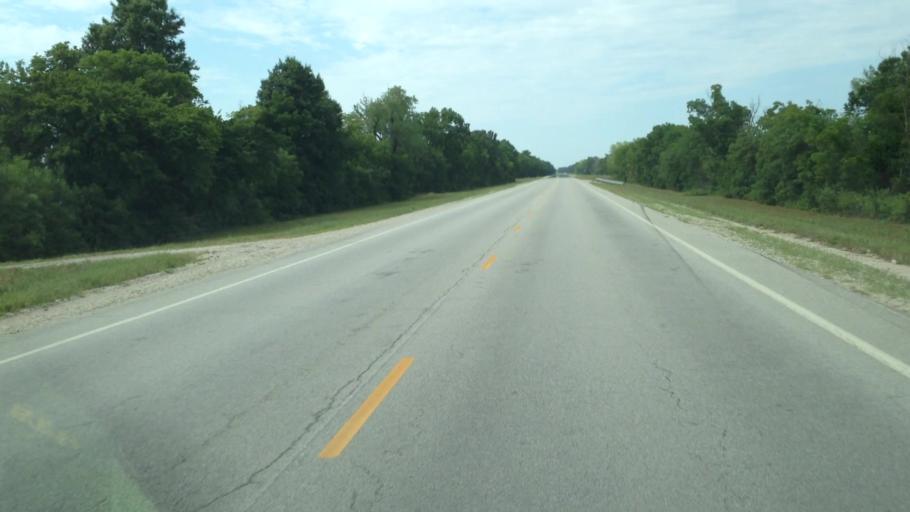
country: US
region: Kansas
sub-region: Labette County
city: Chetopa
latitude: 37.0586
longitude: -95.1027
